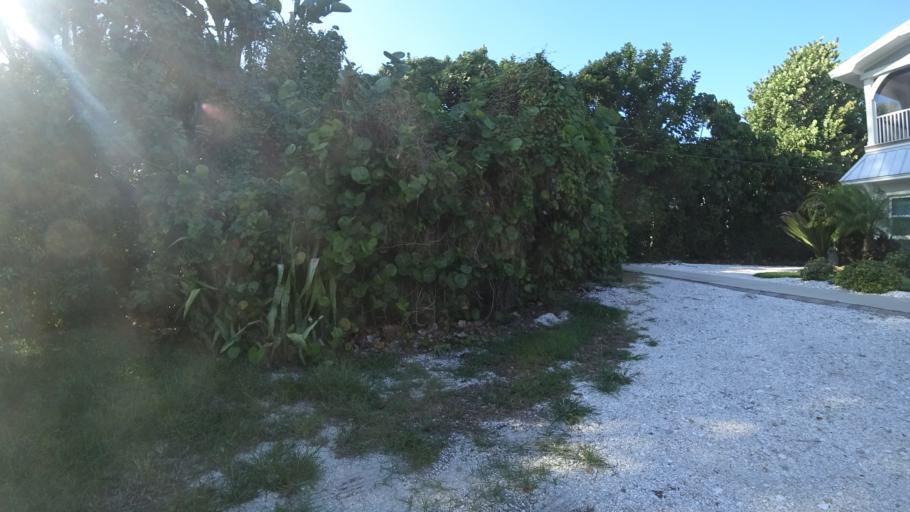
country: US
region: Florida
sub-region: Manatee County
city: Anna Maria
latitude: 27.5214
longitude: -82.7316
